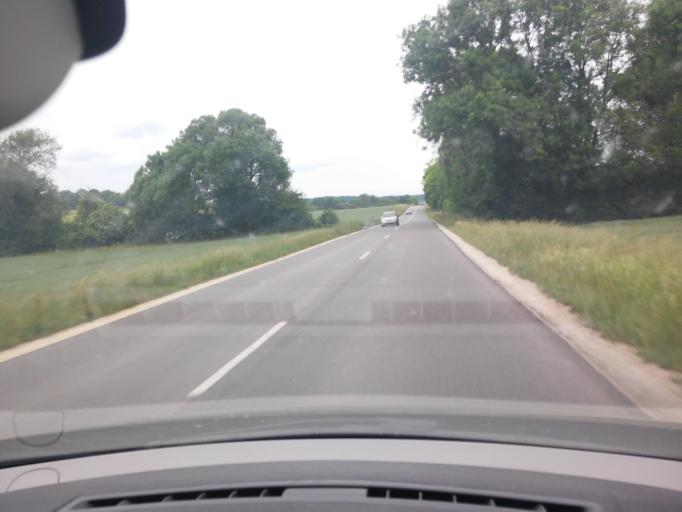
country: FR
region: Lorraine
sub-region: Departement de la Meuse
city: Lerouville
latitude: 48.8123
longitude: 5.5188
